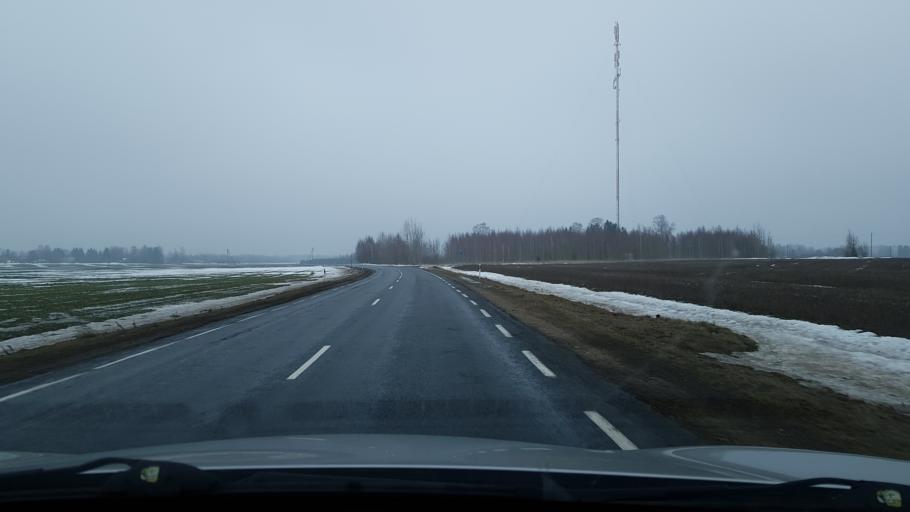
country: EE
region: Valgamaa
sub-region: Torva linn
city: Torva
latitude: 58.1559
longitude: 25.9641
